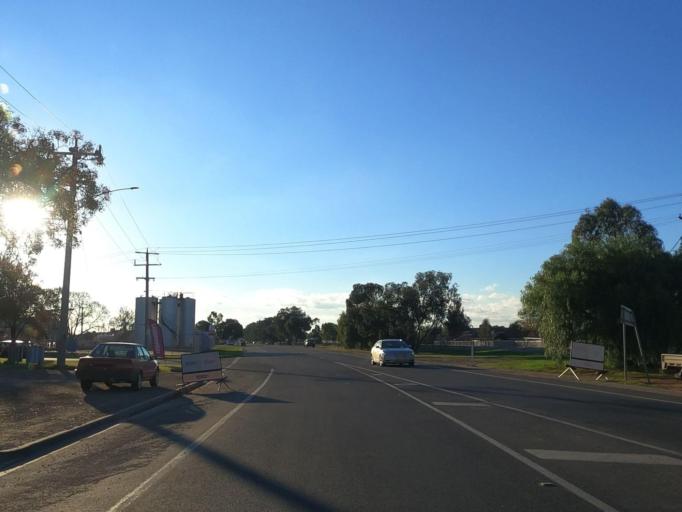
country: AU
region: Victoria
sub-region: Swan Hill
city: Swan Hill
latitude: -35.3341
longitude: 143.5594
